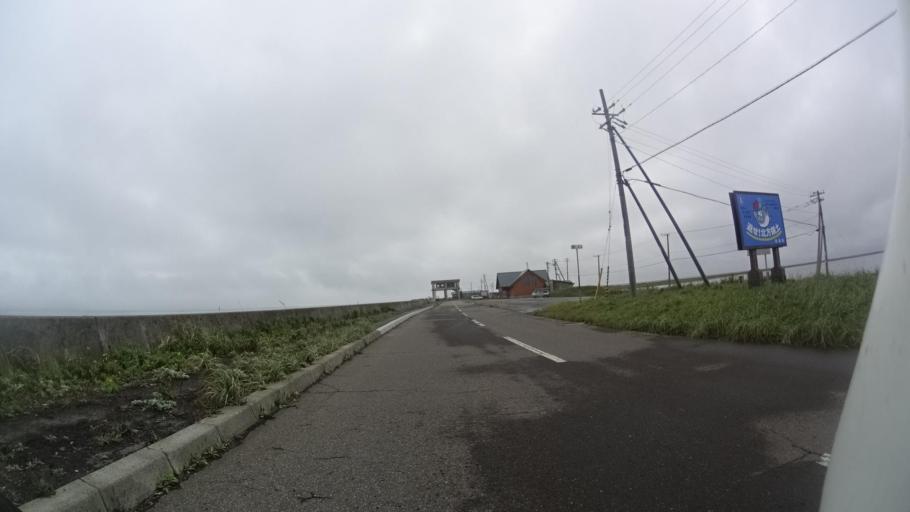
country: JP
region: Hokkaido
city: Shibetsu
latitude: 43.5916
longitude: 145.3337
